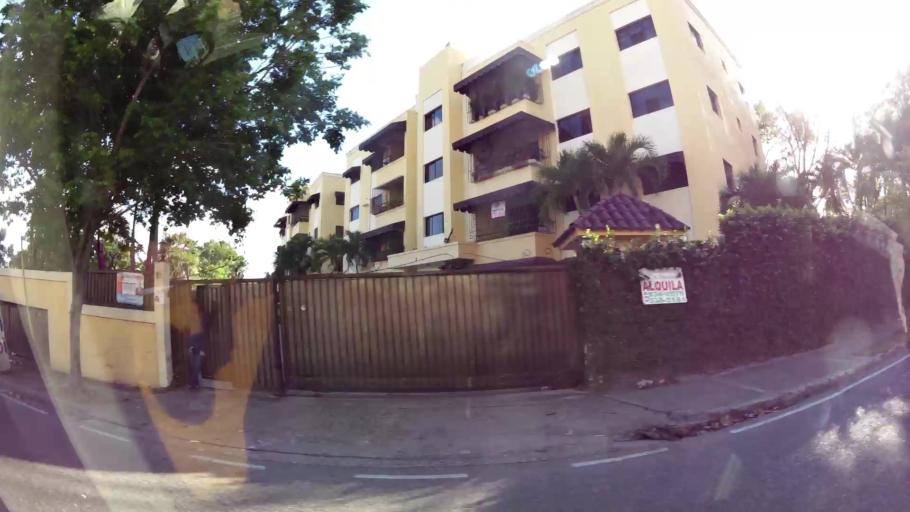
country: DO
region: Nacional
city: La Agustina
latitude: 18.5069
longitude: -69.9601
